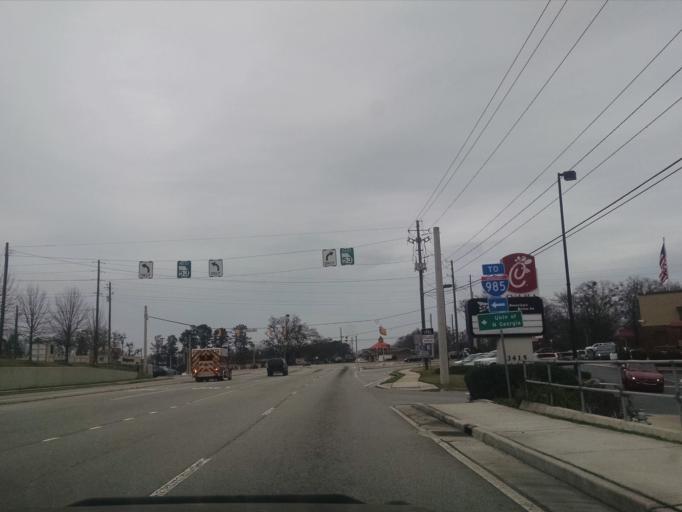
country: US
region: Georgia
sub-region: Hall County
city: Oakwood
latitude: 34.2199
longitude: -83.8635
